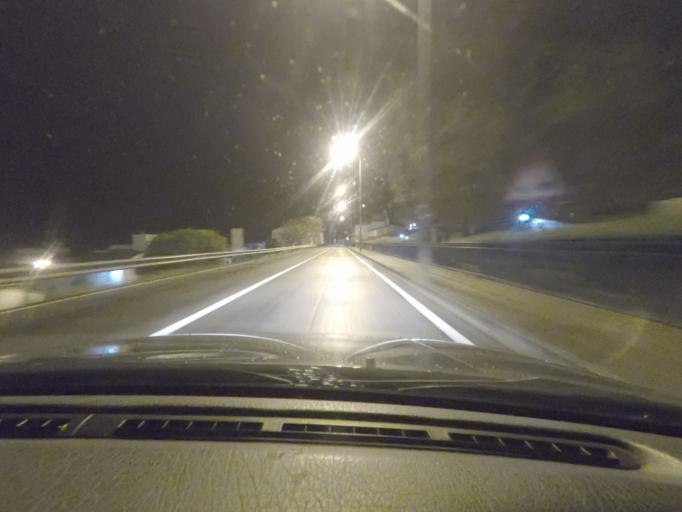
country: ES
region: Extremadura
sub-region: Provincia de Caceres
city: Canaveral
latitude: 39.7939
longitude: -6.3864
